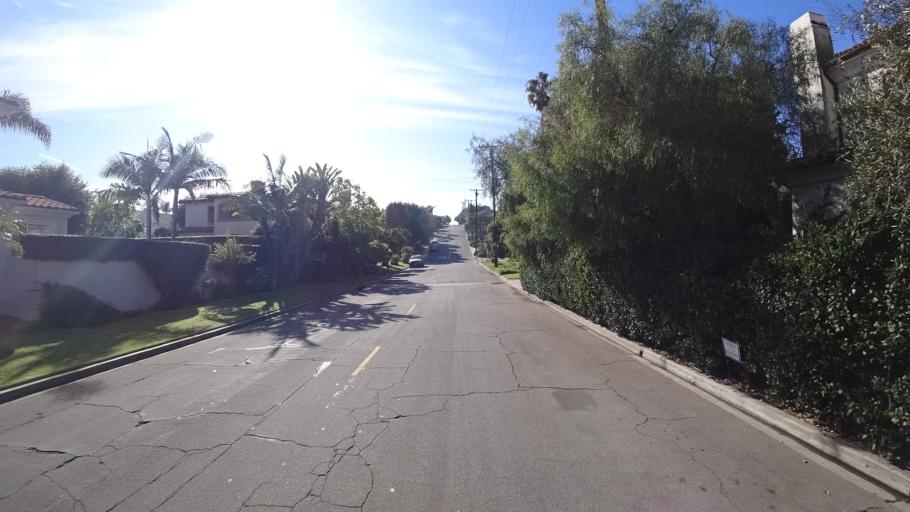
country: US
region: California
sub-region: Los Angeles County
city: Manhattan Beach
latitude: 33.8863
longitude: -118.4004
